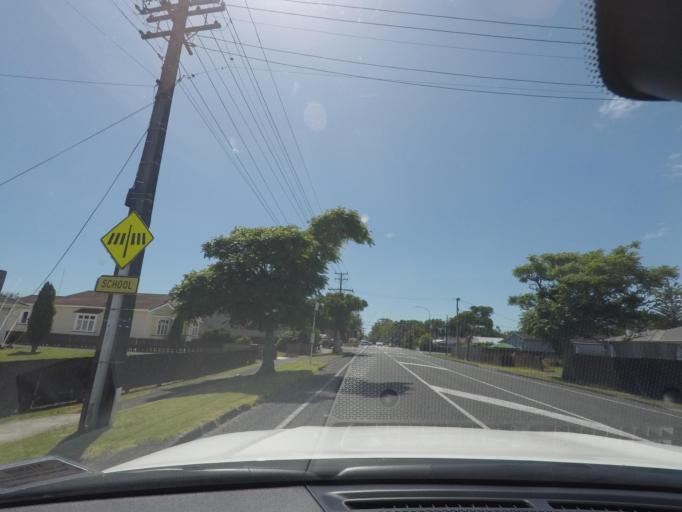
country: NZ
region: Auckland
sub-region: Auckland
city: Parakai
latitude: -36.6622
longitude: 174.4347
